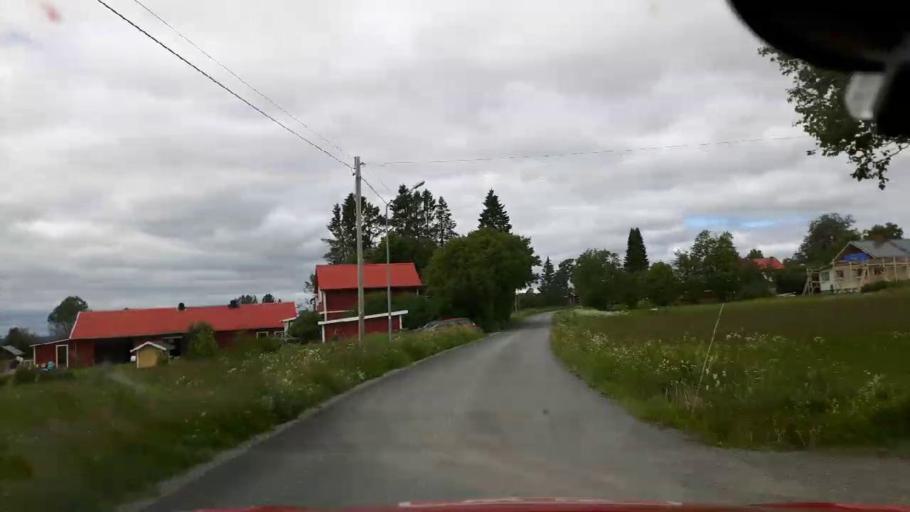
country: SE
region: Jaemtland
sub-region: OEstersunds Kommun
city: Brunflo
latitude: 63.0717
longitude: 14.8895
